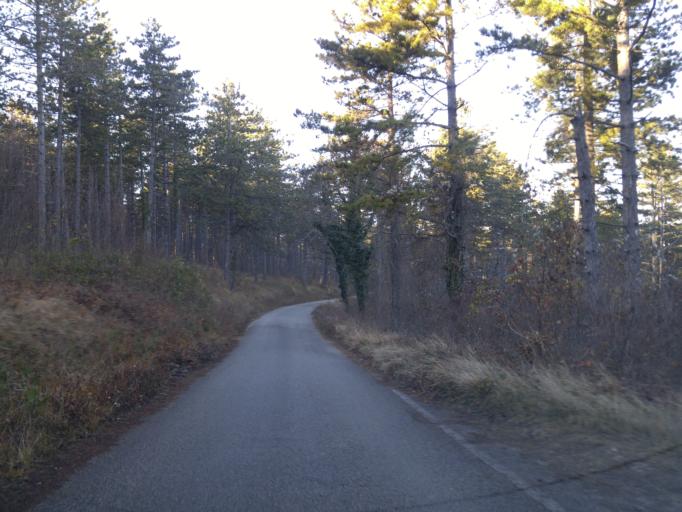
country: IT
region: The Marches
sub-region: Provincia di Pesaro e Urbino
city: Isola del Piano
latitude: 43.7007
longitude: 12.7632
